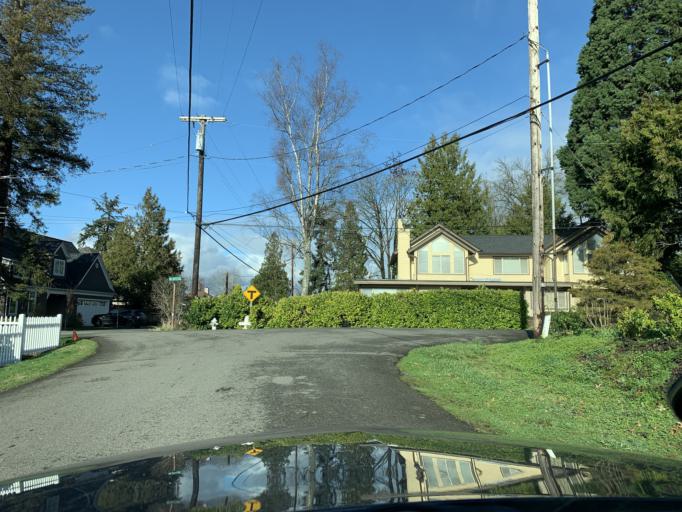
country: US
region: Washington
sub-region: King County
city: Mercer Island
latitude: 47.5869
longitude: -122.2498
